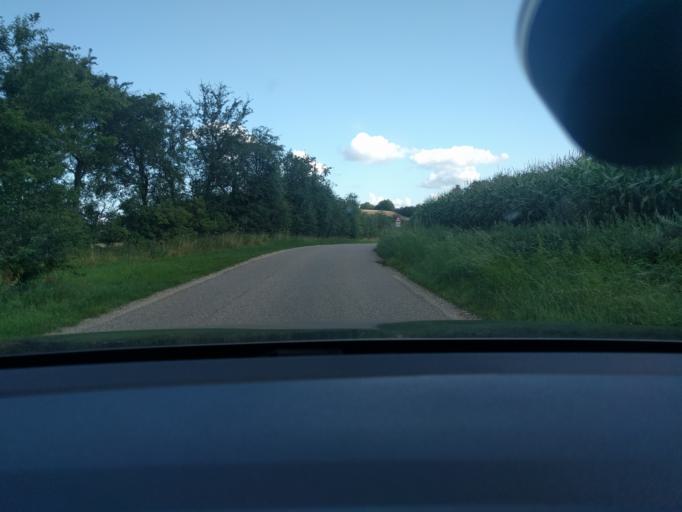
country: DK
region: Central Jutland
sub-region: Viborg Kommune
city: Viborg
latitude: 56.5245
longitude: 9.3250
